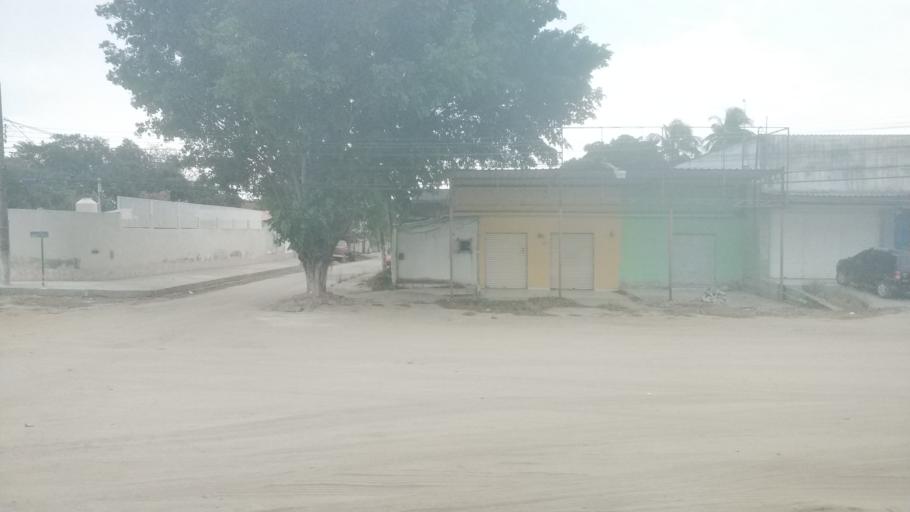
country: BR
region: Rio de Janeiro
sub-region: Seropedica
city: Seropedica
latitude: -22.8000
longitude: -43.6442
